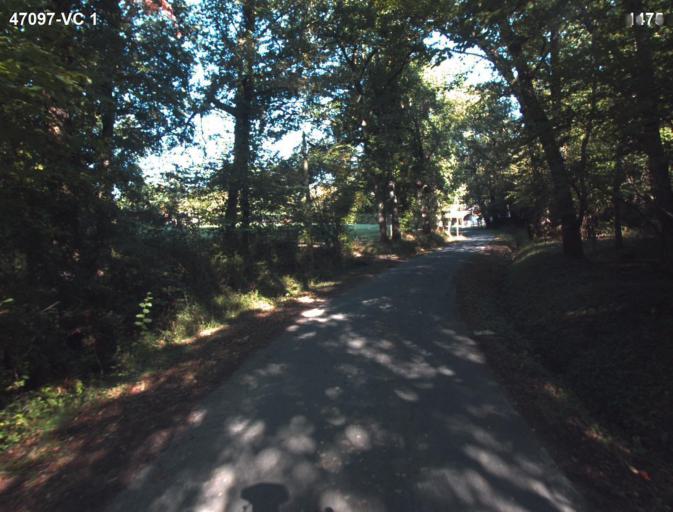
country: FR
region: Aquitaine
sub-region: Departement du Lot-et-Garonne
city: Vianne
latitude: 44.2114
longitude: 0.3568
